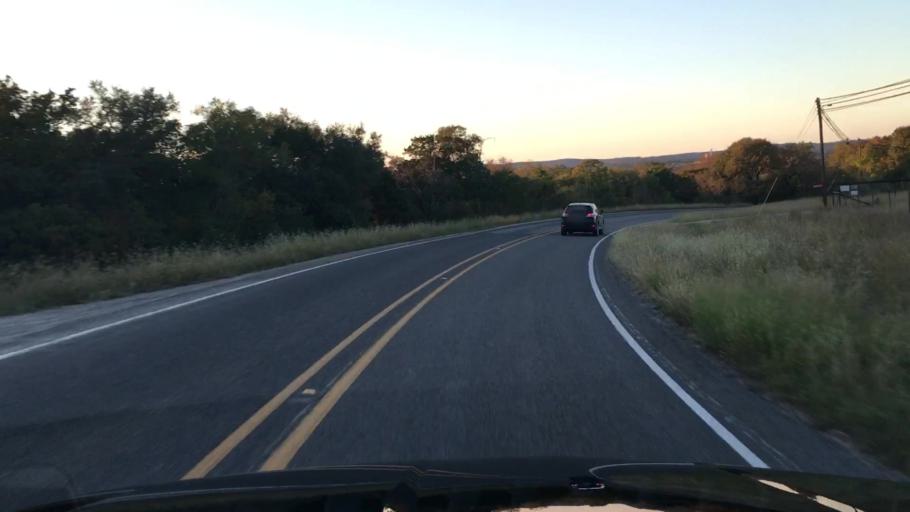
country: US
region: Texas
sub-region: Blanco County
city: Blanco
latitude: 30.0833
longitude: -98.4136
